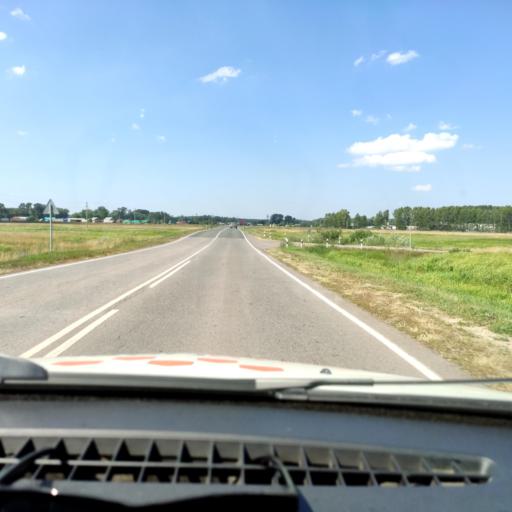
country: RU
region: Bashkortostan
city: Alekseyevka
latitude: 55.0684
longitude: 55.0916
